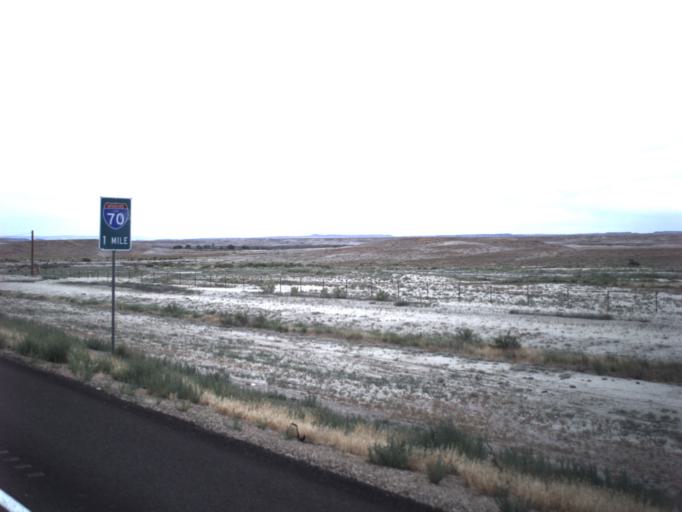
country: US
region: Utah
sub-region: Carbon County
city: East Carbon City
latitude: 38.9936
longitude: -110.2545
